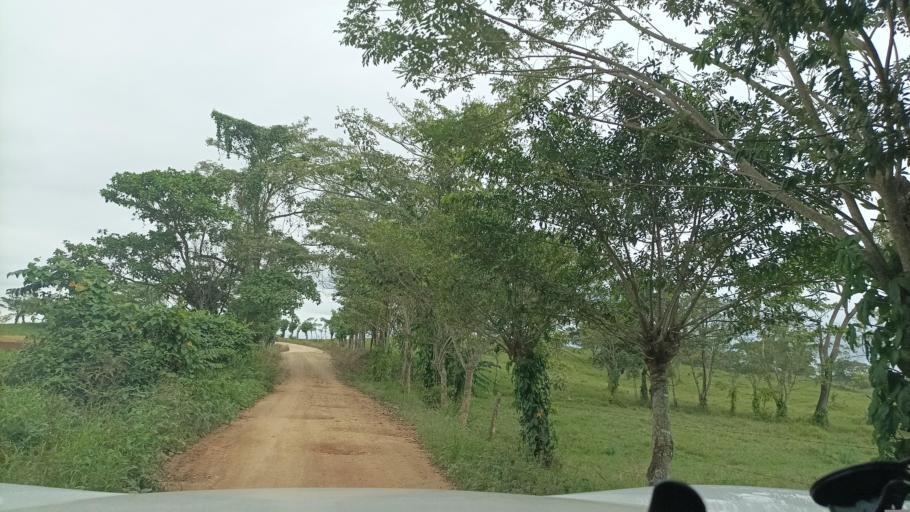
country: MX
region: Veracruz
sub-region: Texistepec
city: Venustiano Carranza (Pena Blanca)
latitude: 17.5089
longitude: -94.5620
